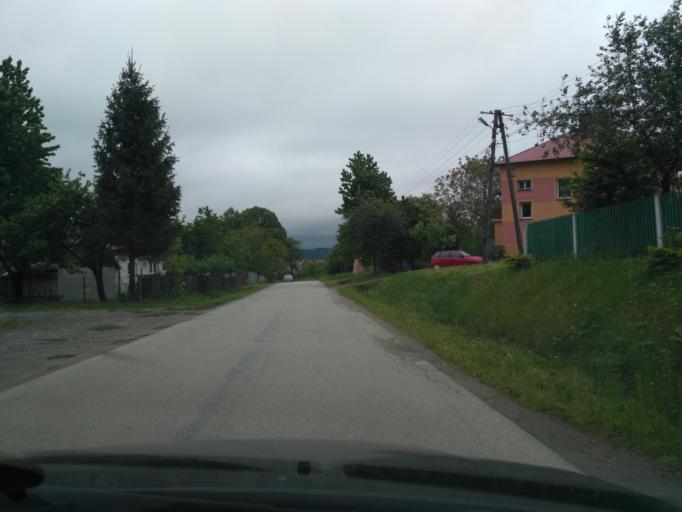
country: PL
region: Subcarpathian Voivodeship
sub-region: Powiat jasielski
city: Brzyska
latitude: 49.8199
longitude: 21.3656
